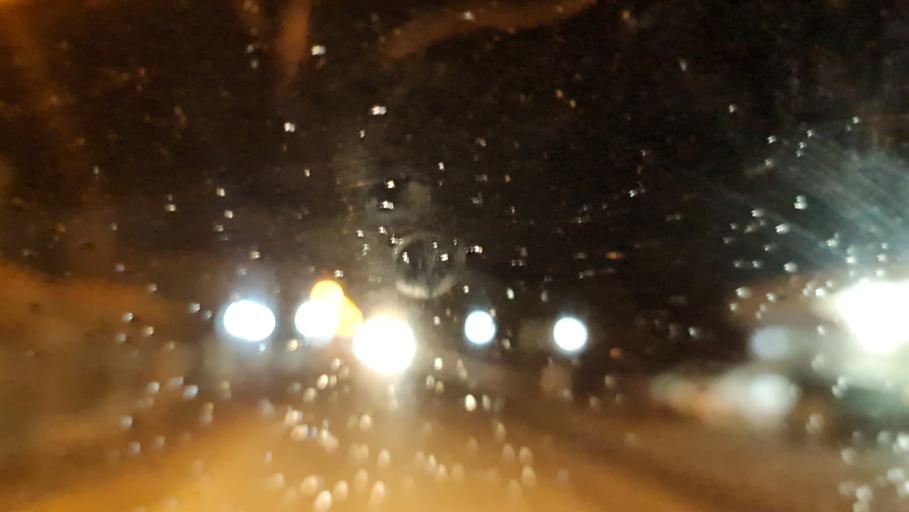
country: MZ
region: Nampula
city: Nampula
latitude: -15.1125
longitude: 39.2871
